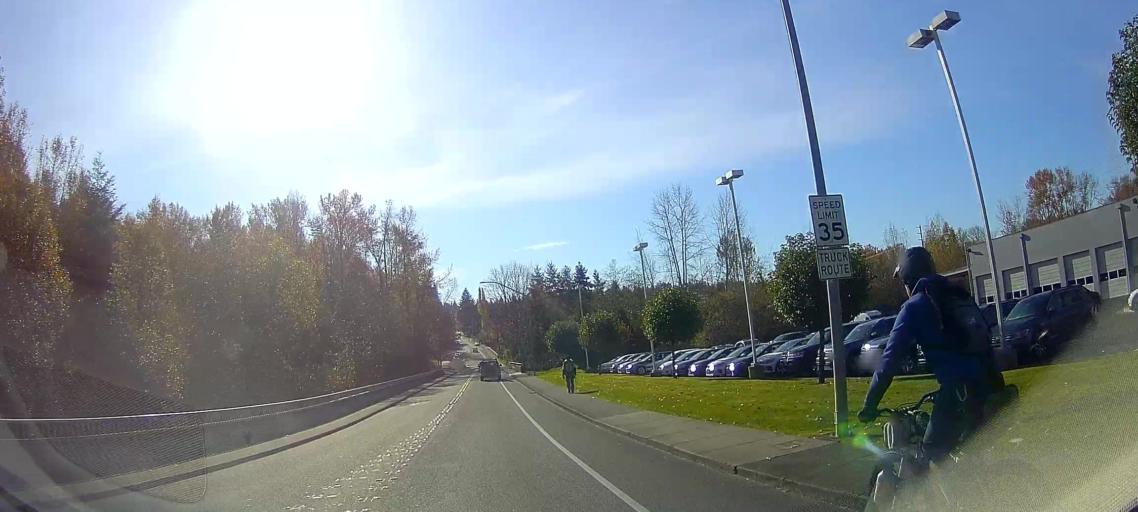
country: US
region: Washington
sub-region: Whatcom County
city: Bellingham
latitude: 48.7558
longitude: -122.4453
